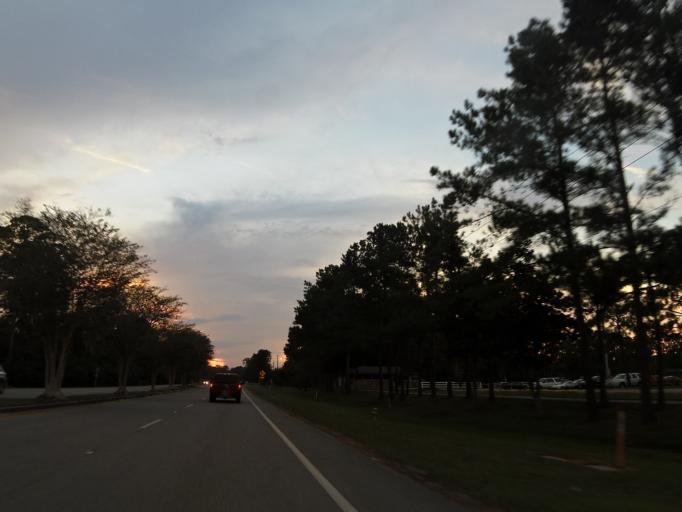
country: US
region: Florida
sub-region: Saint Johns County
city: Fruit Cove
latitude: 30.1204
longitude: -81.6188
